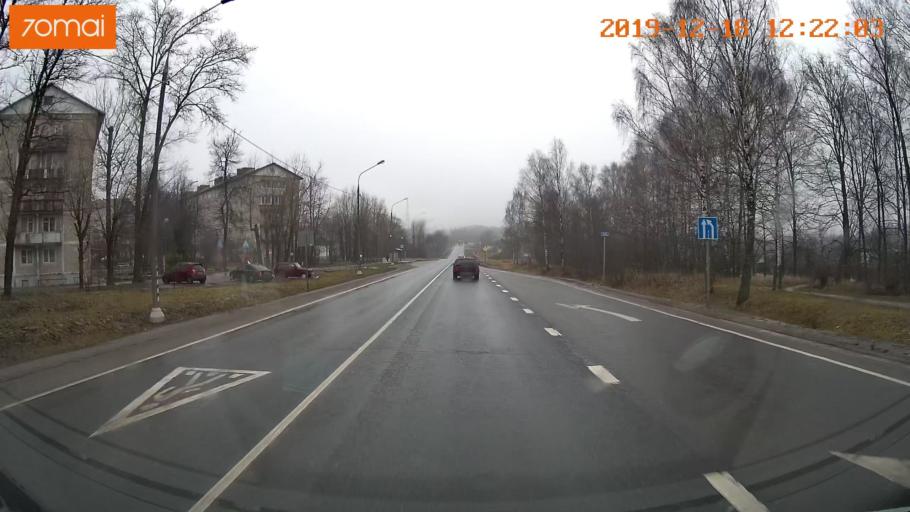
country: RU
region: Moskovskaya
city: Novopetrovskoye
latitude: 56.0026
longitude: 36.4778
